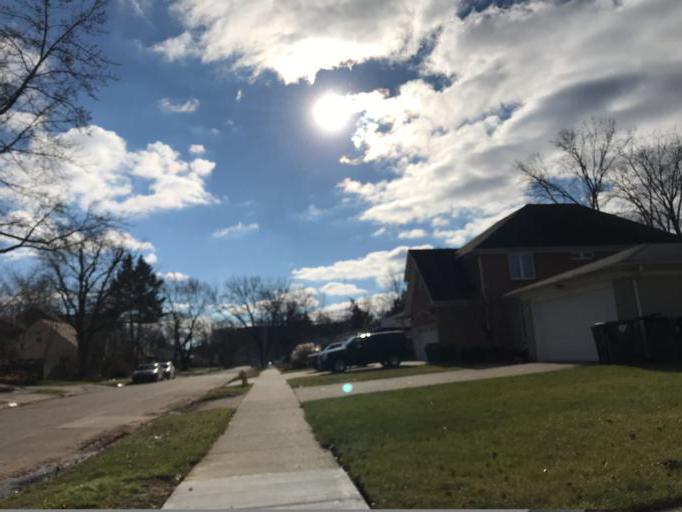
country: US
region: Michigan
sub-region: Oakland County
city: Berkley
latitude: 42.4842
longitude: -83.1980
